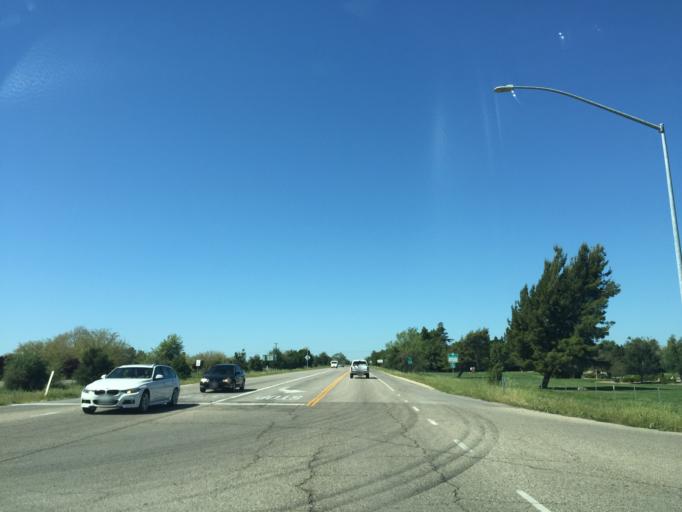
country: US
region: California
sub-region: Santa Barbara County
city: Santa Ynez
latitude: 34.6337
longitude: -120.0810
